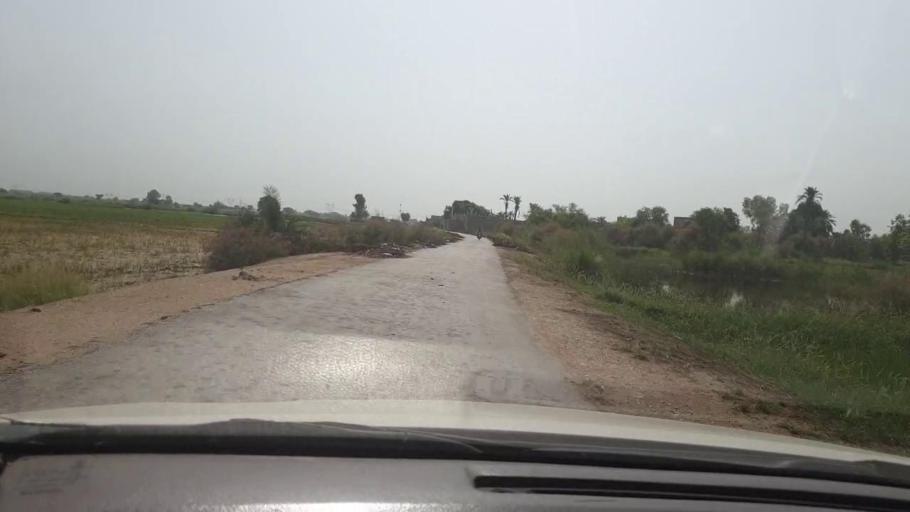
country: PK
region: Sindh
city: Rustam jo Goth
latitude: 27.9773
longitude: 68.7993
